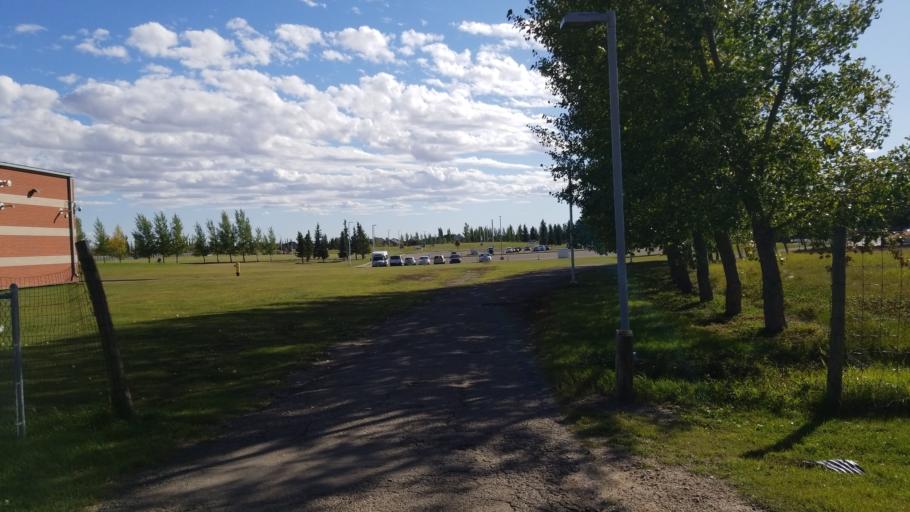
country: CA
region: Saskatchewan
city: Lloydminster
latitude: 53.2624
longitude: -110.0317
